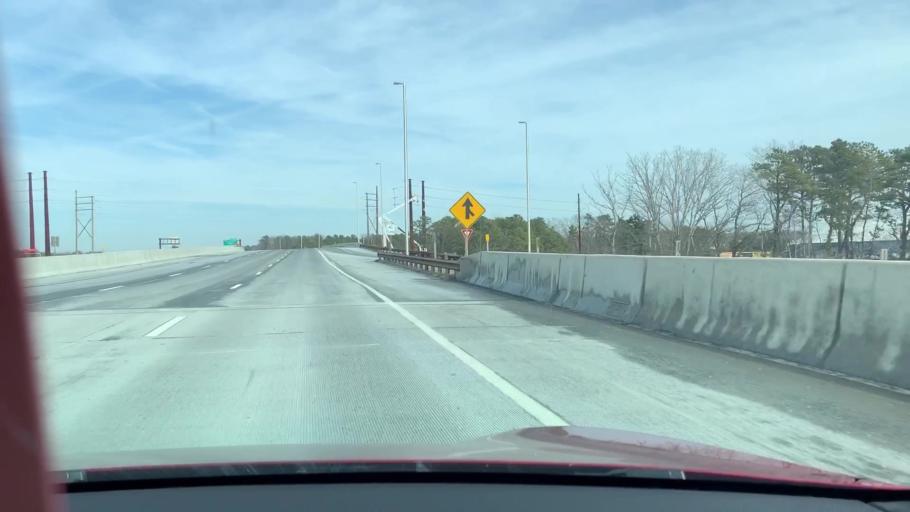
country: US
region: New Jersey
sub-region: Atlantic County
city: Northfield
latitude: 39.4003
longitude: -74.5594
